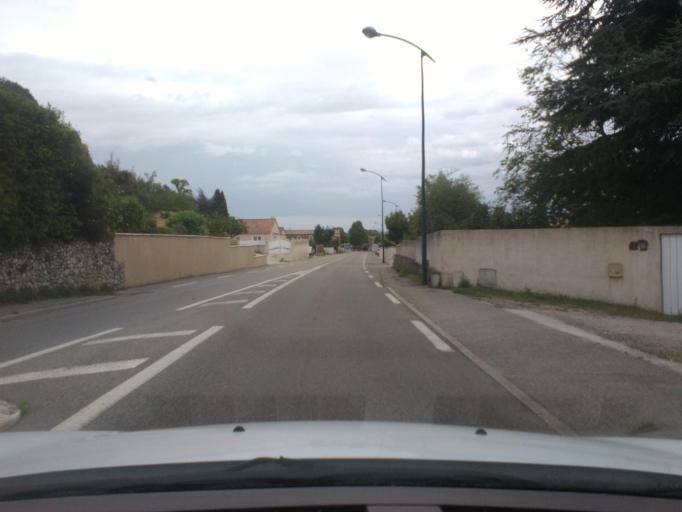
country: FR
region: Rhone-Alpes
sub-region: Departement de l'Ardeche
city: Cornas
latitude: 44.9699
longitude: 4.8508
